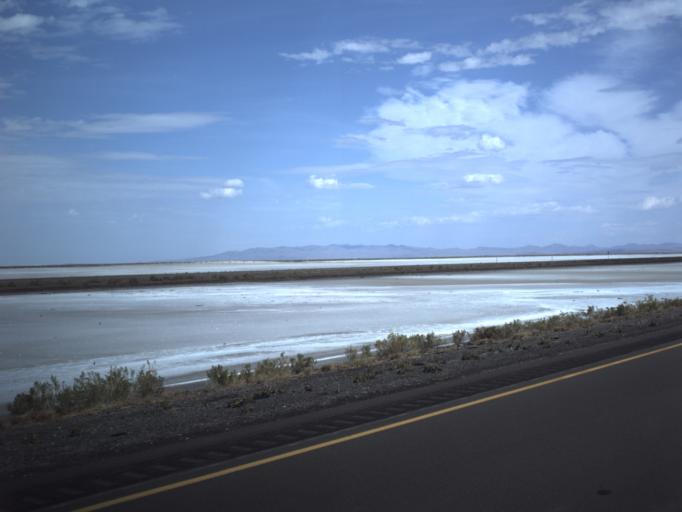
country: US
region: Utah
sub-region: Tooele County
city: Wendover
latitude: 40.7295
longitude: -113.4392
